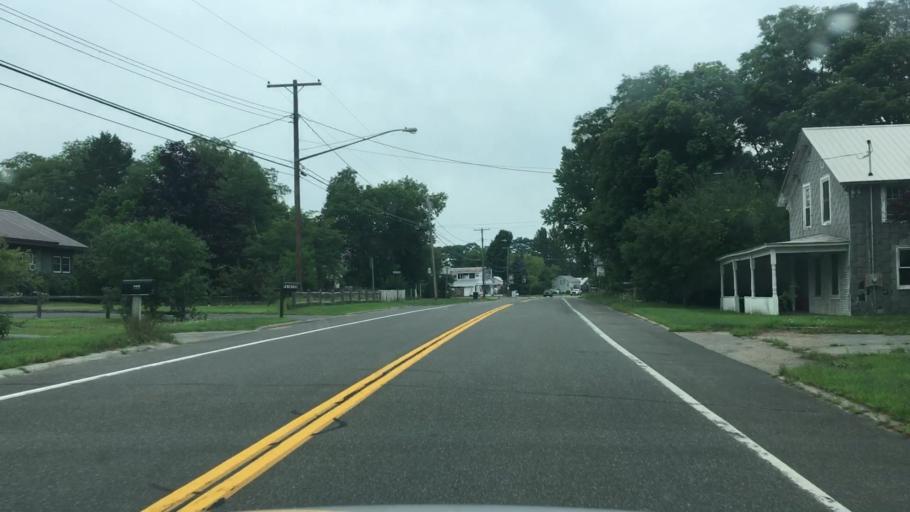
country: US
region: New York
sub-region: Essex County
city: Keeseville
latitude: 44.4999
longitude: -73.4939
